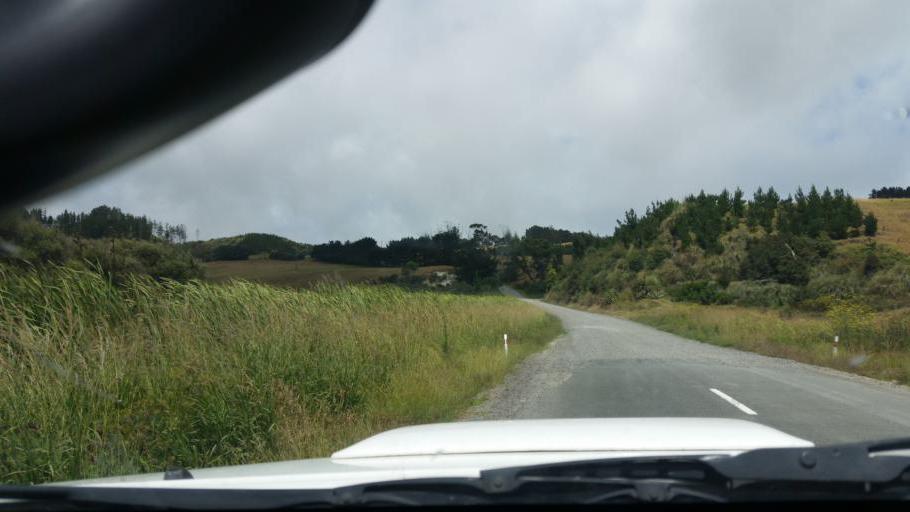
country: NZ
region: Northland
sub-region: Kaipara District
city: Dargaville
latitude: -35.8349
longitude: 173.6611
